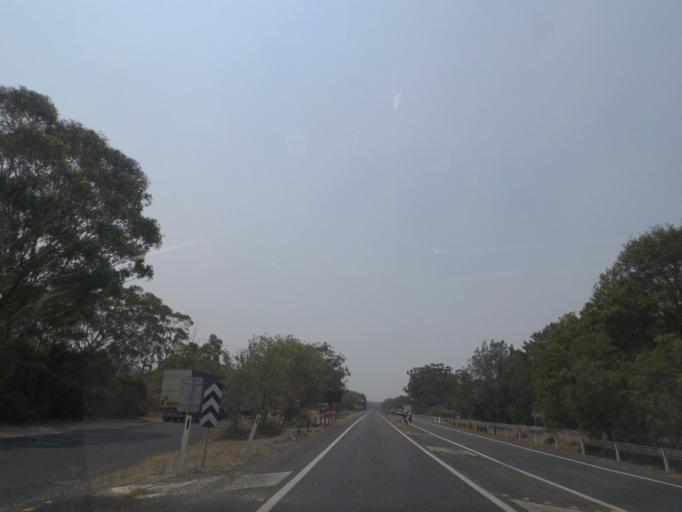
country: AU
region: New South Wales
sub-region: Ballina
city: Ballina
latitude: -28.9351
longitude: 153.4718
